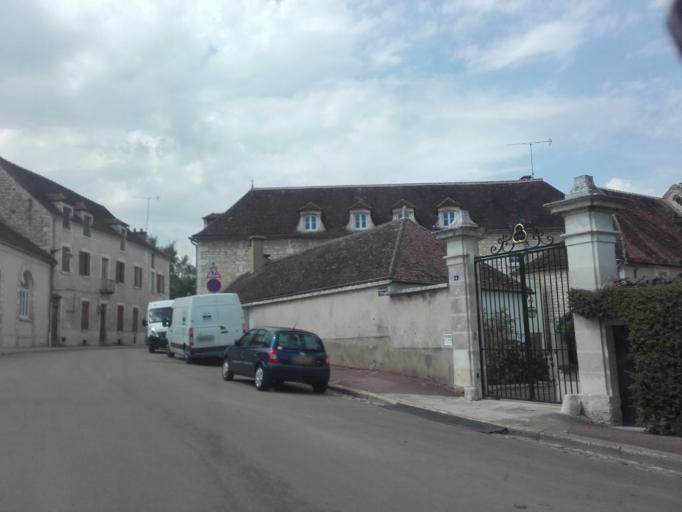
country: FR
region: Bourgogne
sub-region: Departement de l'Yonne
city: Chablis
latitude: 47.8138
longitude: 3.8006
